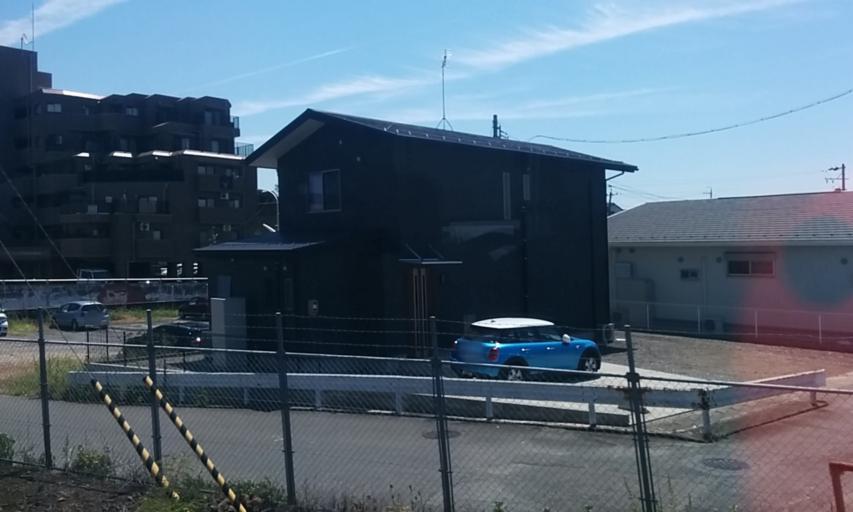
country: JP
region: Gifu
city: Gifu-shi
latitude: 35.4055
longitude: 136.7268
